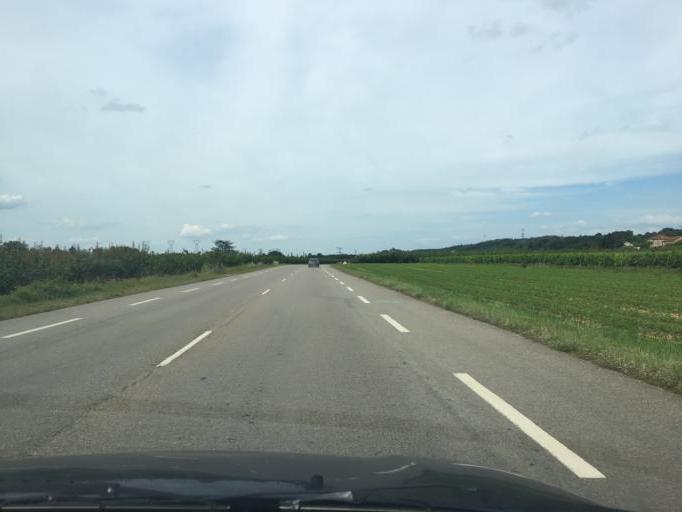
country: FR
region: Rhone-Alpes
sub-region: Departement de la Drome
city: Beaumont-Monteux
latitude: 44.9957
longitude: 4.9148
